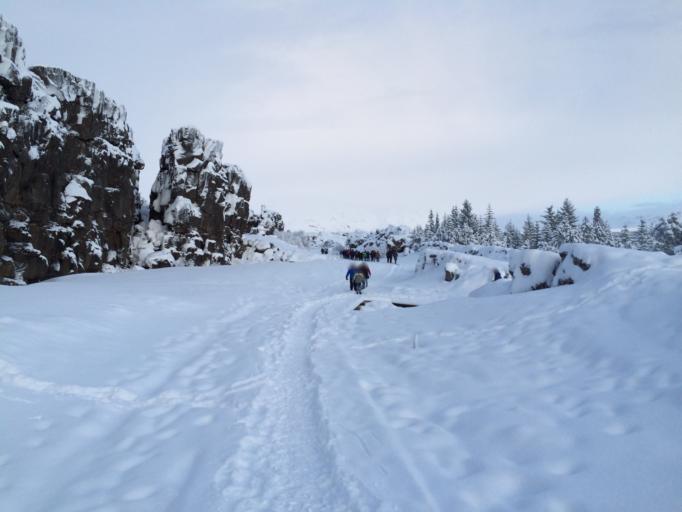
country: IS
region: South
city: Hveragerdi
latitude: 64.2669
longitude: -21.1161
